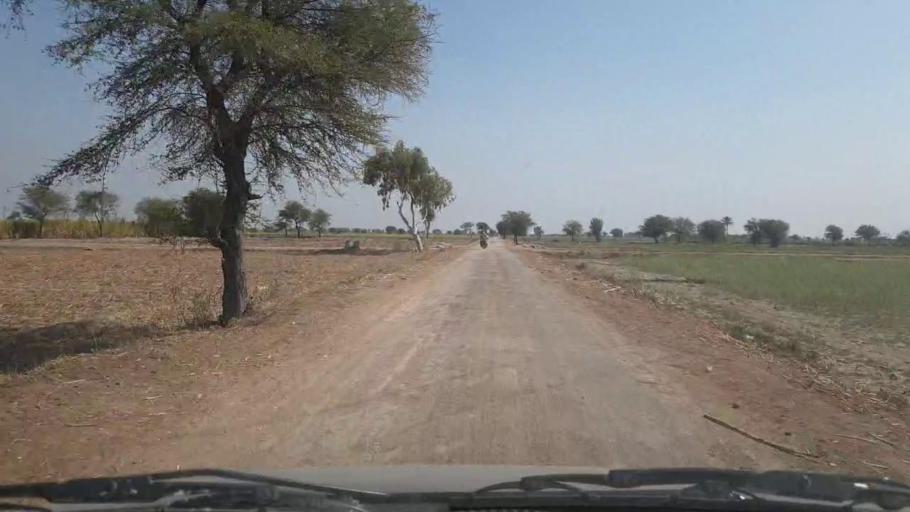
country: PK
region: Sindh
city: Samaro
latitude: 25.2455
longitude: 69.3628
